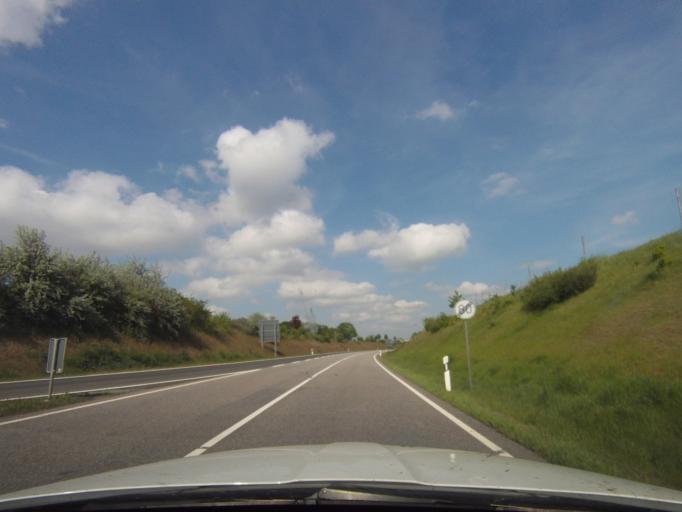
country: DE
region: Thuringia
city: Triptis
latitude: 50.7516
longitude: 11.8768
